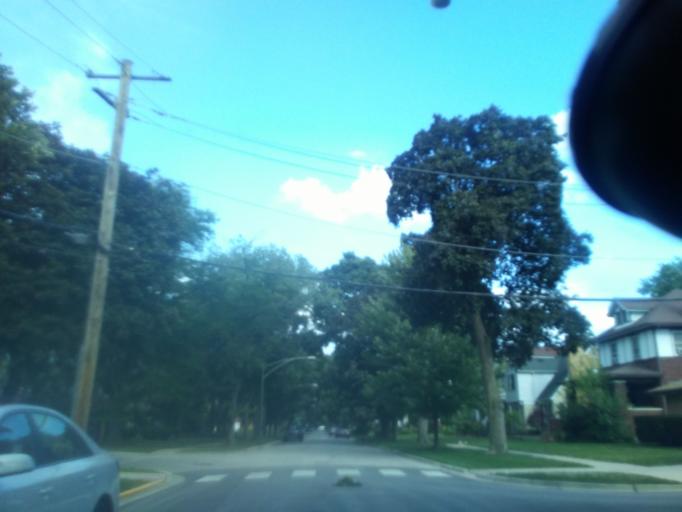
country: US
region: Illinois
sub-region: Cook County
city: Lincolnwood
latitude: 41.9799
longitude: -87.7539
